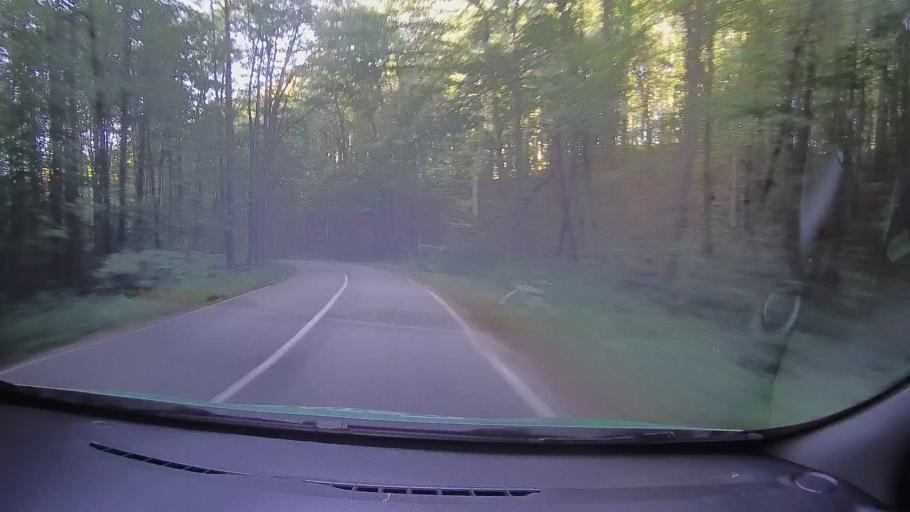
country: RO
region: Timis
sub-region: Comuna Nadrag
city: Nadrag
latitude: 45.6855
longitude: 22.1580
